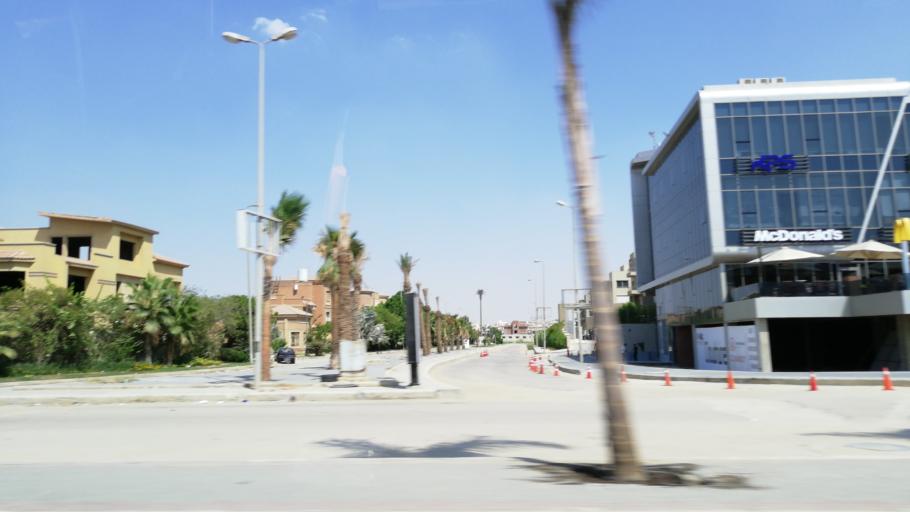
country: EG
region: Muhafazat al Qalyubiyah
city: Al Khankah
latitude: 30.0502
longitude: 31.4751
